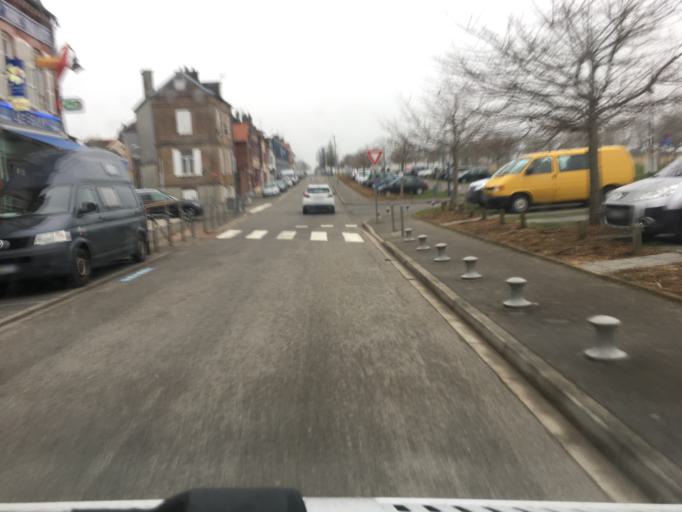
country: FR
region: Picardie
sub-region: Departement de la Somme
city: Saint-Valery-sur-Somme
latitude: 50.1794
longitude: 1.6438
